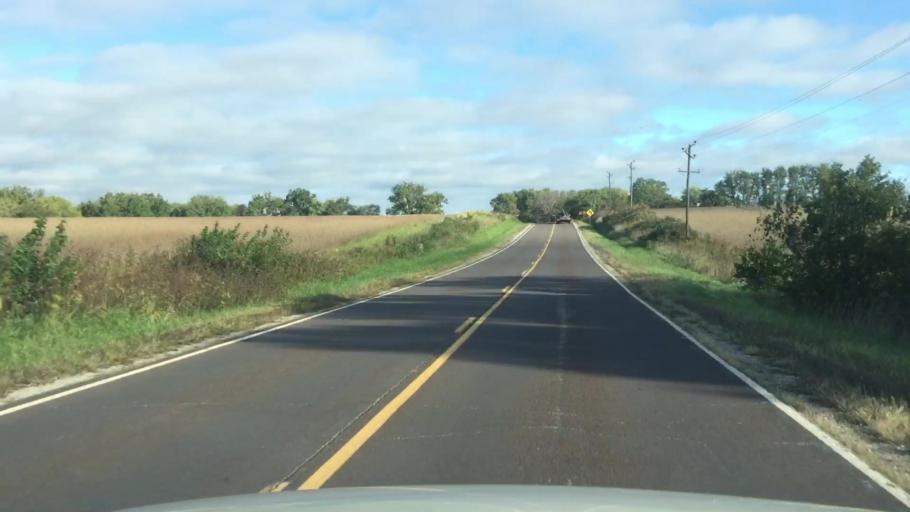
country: US
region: Missouri
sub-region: Howard County
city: New Franklin
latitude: 39.0579
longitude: -92.7442
